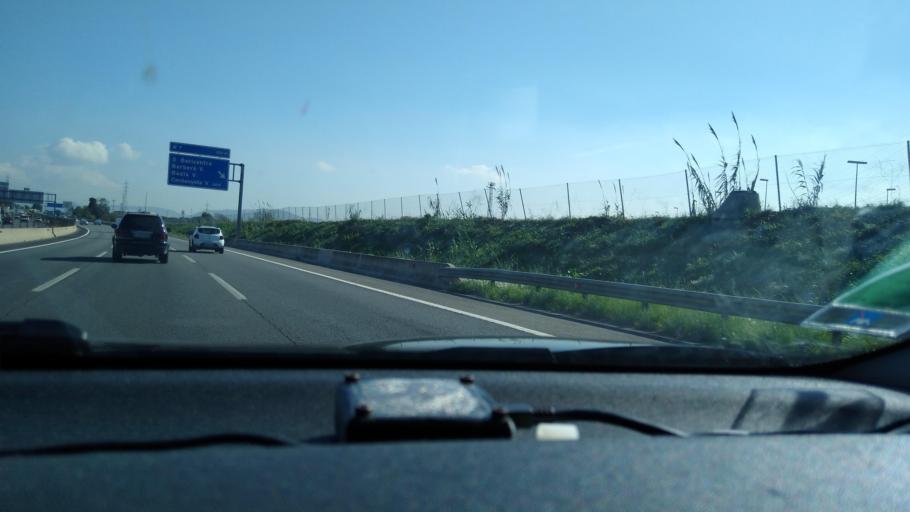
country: ES
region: Catalonia
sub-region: Provincia de Barcelona
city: Barbera del Valles
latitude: 41.5042
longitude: 2.1190
